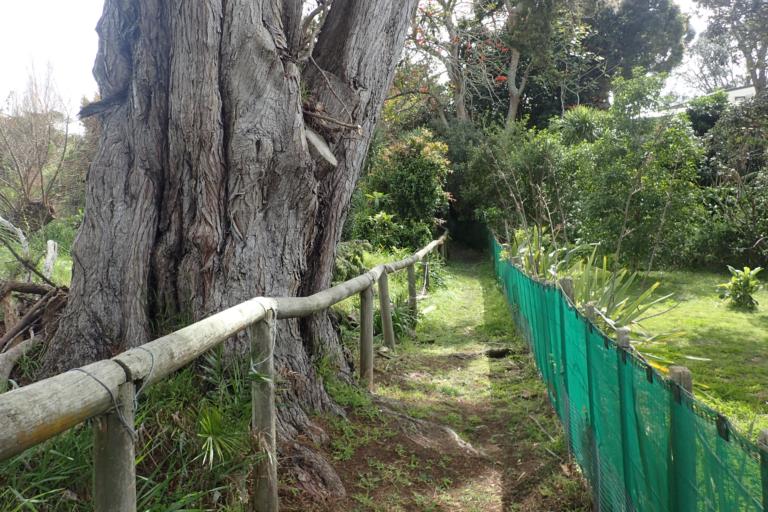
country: NZ
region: Auckland
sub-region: Auckland
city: Pakuranga
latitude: -36.7882
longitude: 175.0080
